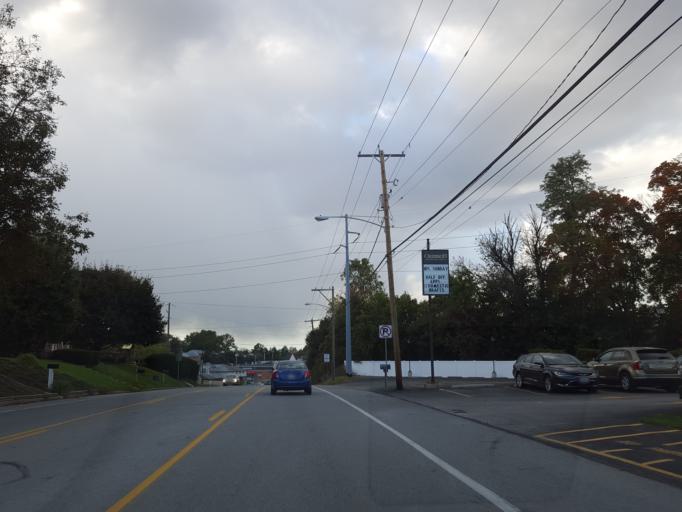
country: US
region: Pennsylvania
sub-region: York County
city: Valley View
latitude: 39.9409
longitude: -76.7012
